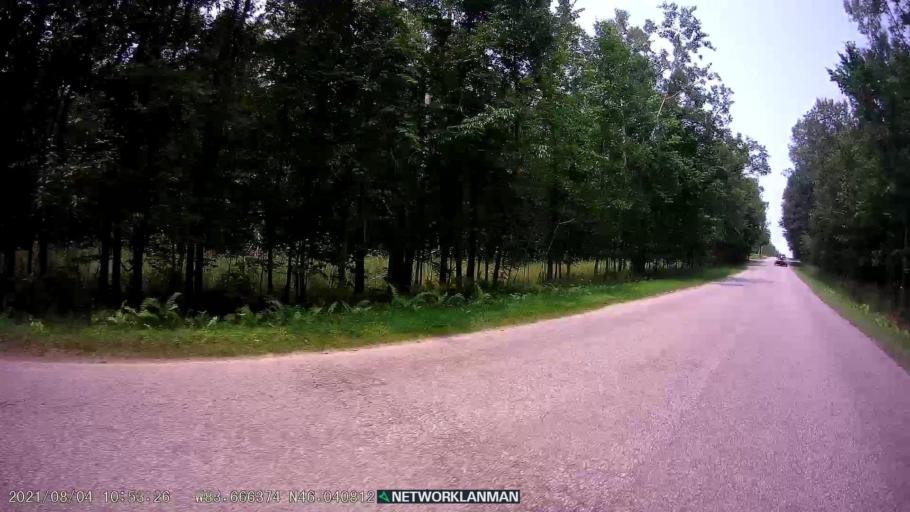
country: CA
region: Ontario
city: Thessalon
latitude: 46.0415
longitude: -83.6673
